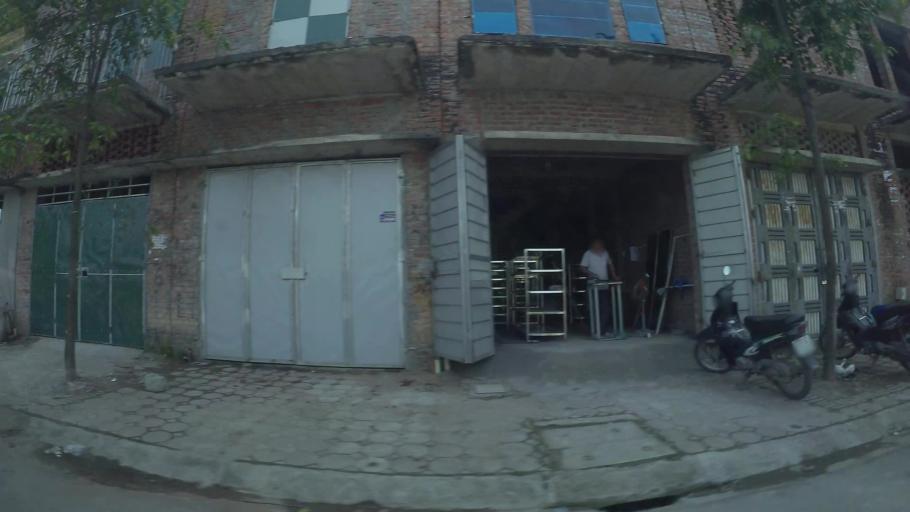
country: VN
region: Ha Noi
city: Ha Dong
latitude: 20.9713
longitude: 105.7995
